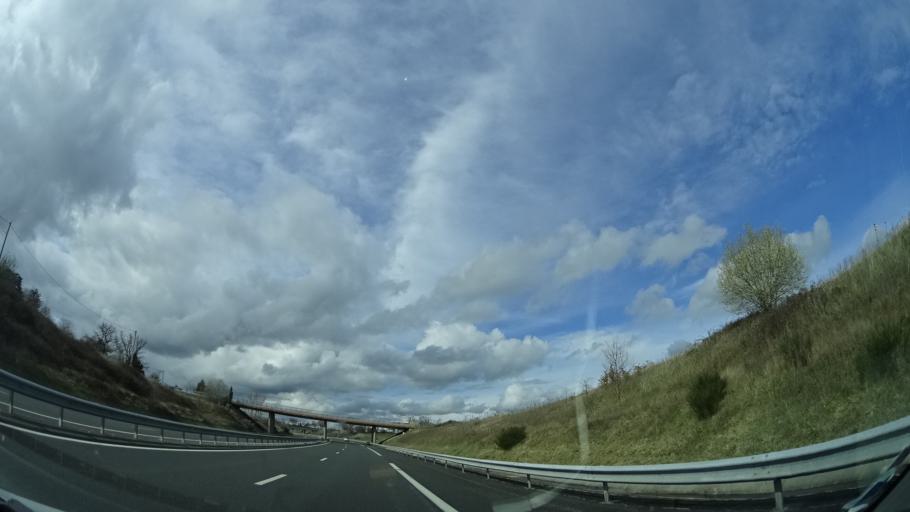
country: FR
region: Rhone-Alpes
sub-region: Departement de la Loire
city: La Pacaudiere
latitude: 46.1769
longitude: 3.8795
